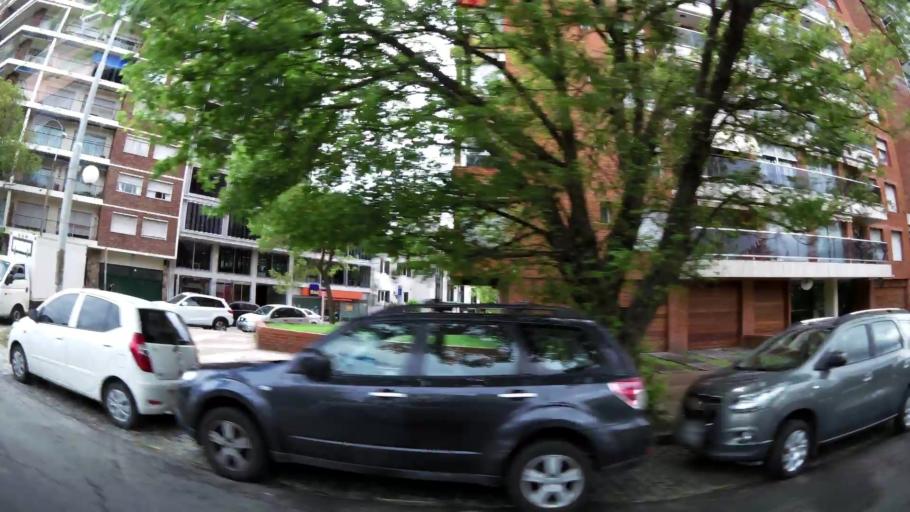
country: UY
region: Montevideo
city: Montevideo
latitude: -34.9235
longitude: -56.1616
